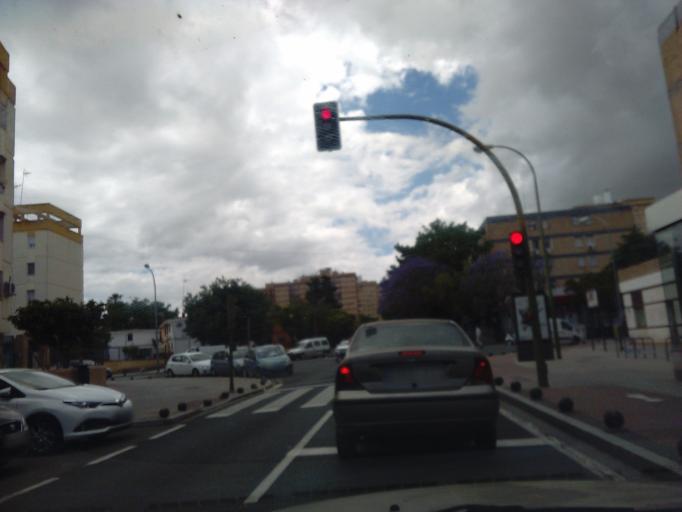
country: ES
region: Andalusia
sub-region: Provincia de Sevilla
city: Sevilla
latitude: 37.3761
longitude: -5.9526
